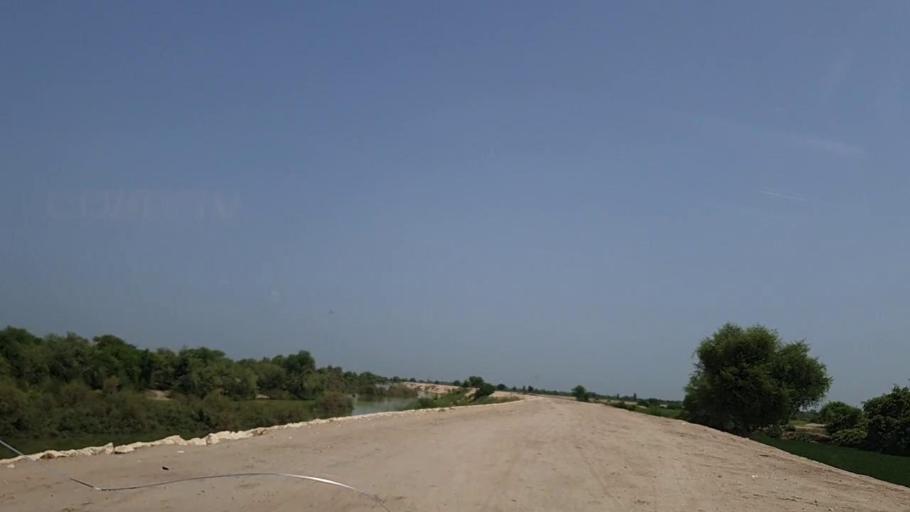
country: PK
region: Sindh
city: Kandiaro
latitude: 27.0581
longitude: 68.1308
